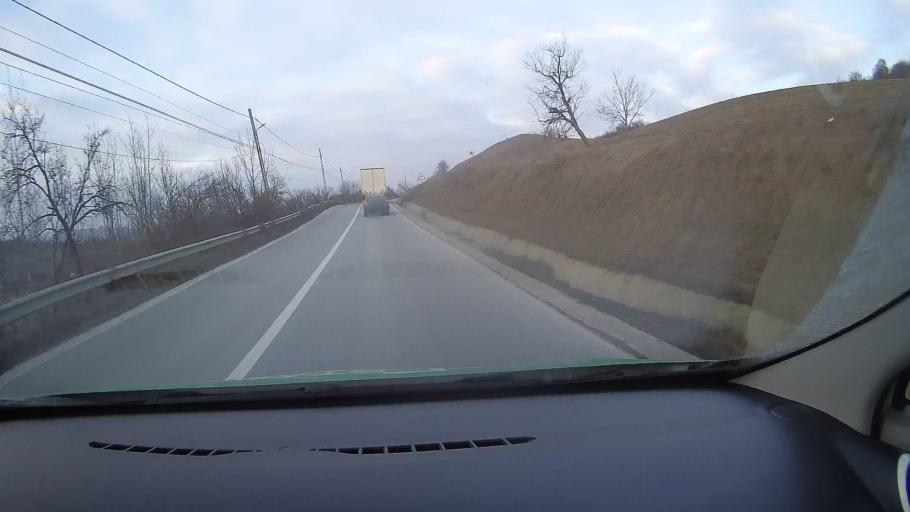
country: RO
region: Harghita
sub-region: Comuna Simonesti
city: Simonesti
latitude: 46.3289
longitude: 25.1038
